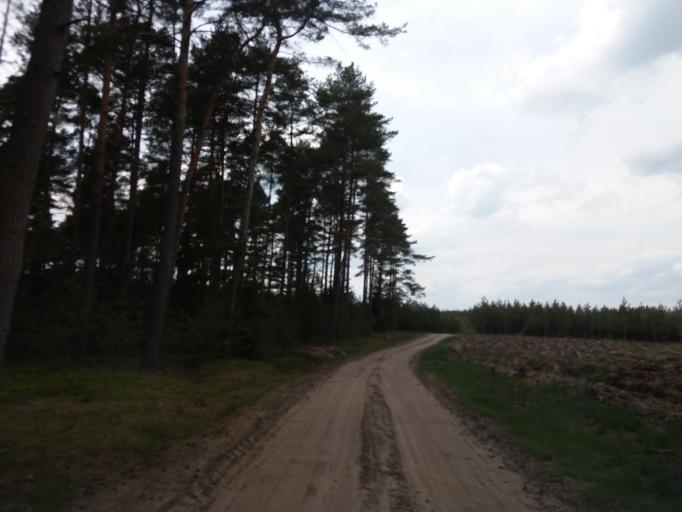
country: PL
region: West Pomeranian Voivodeship
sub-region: Powiat choszczenski
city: Drawno
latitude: 53.1603
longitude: 15.7554
